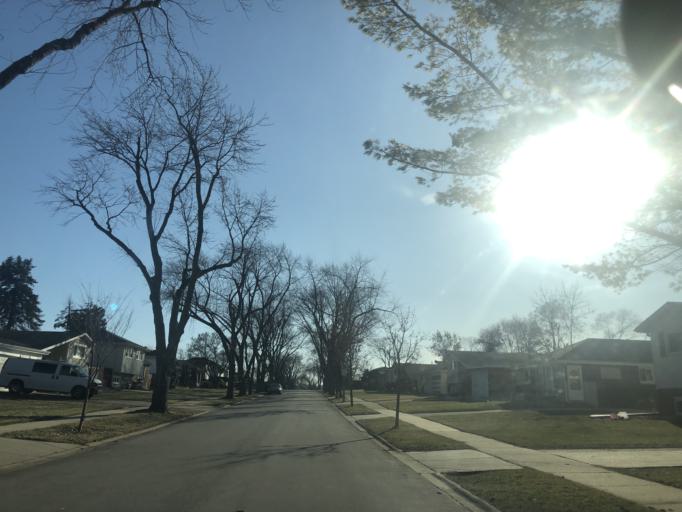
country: US
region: Illinois
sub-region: DuPage County
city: Addison
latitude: 41.9413
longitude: -87.9996
